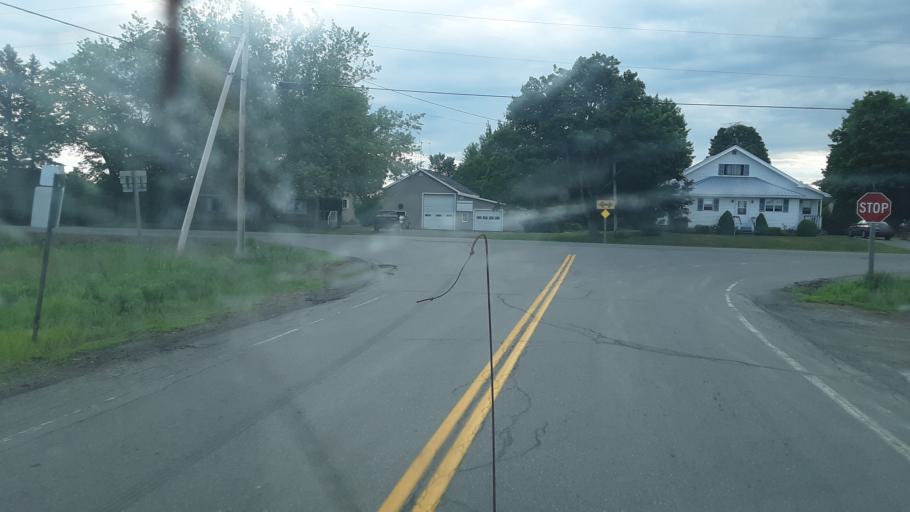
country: US
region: Maine
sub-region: Penobscot County
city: Patten
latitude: 45.8706
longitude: -68.3305
